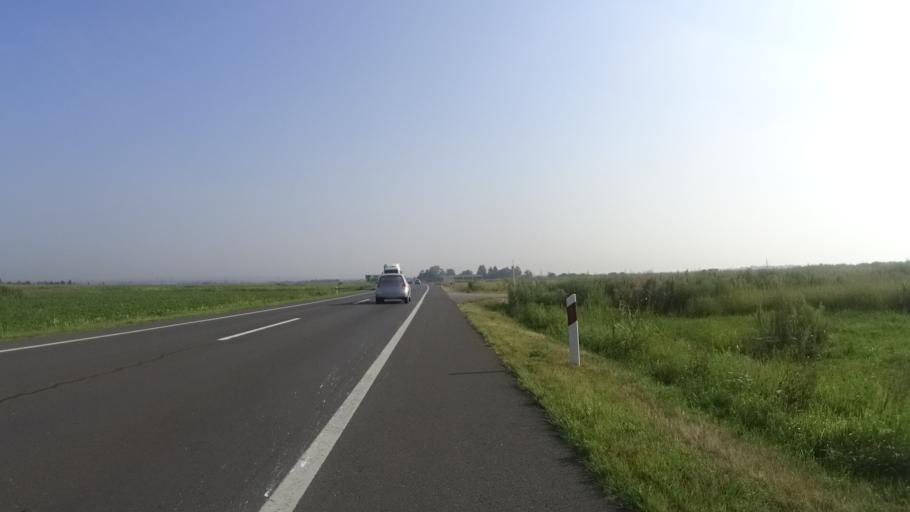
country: HR
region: Medimurska
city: Nedelisce
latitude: 46.3568
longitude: 16.3667
